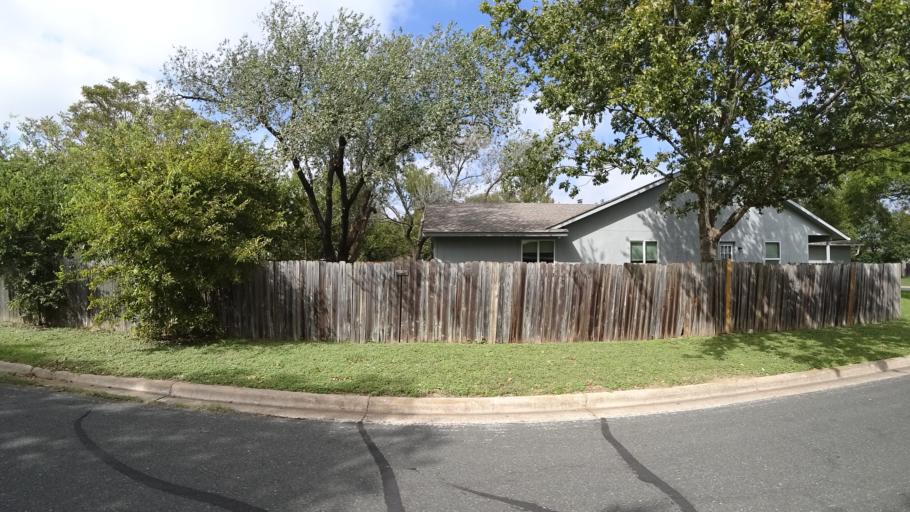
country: US
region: Texas
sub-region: Travis County
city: Shady Hollow
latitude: 30.1995
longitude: -97.8331
